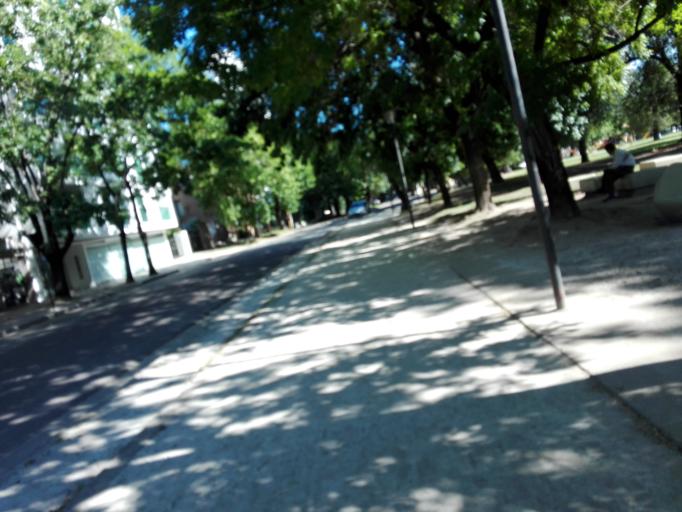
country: AR
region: Buenos Aires
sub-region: Partido de La Plata
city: La Plata
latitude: -34.9313
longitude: -57.9645
